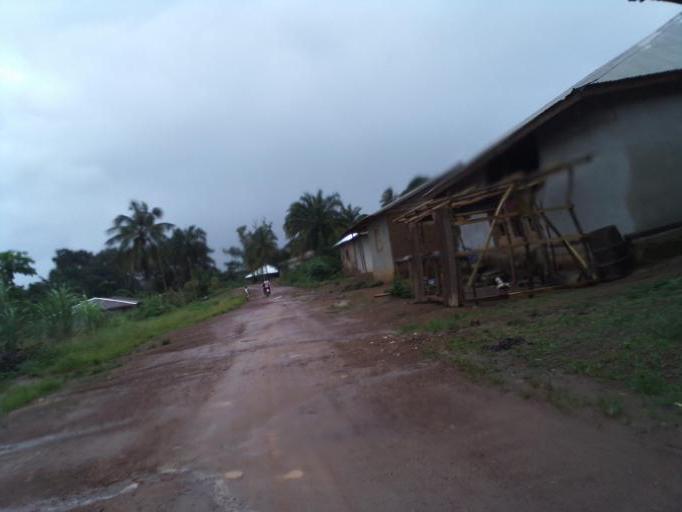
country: SL
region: Eastern Province
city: Kenema
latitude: 7.8813
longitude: -11.1570
